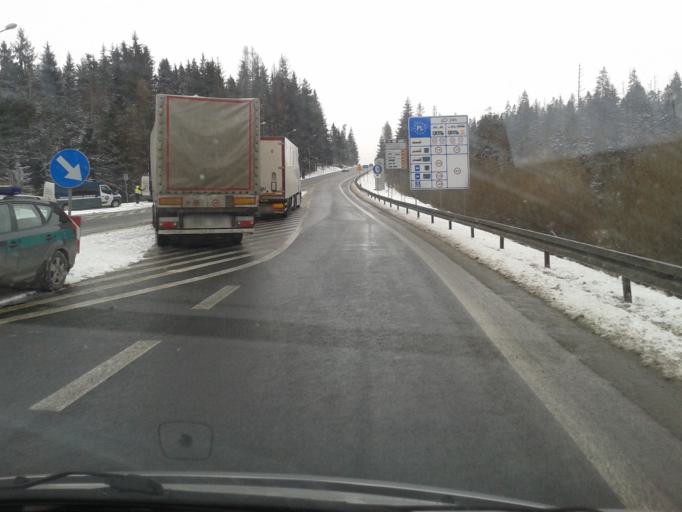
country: PL
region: Lesser Poland Voivodeship
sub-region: Powiat nowotarski
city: Chyzne
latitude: 49.4079
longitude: 19.6587
